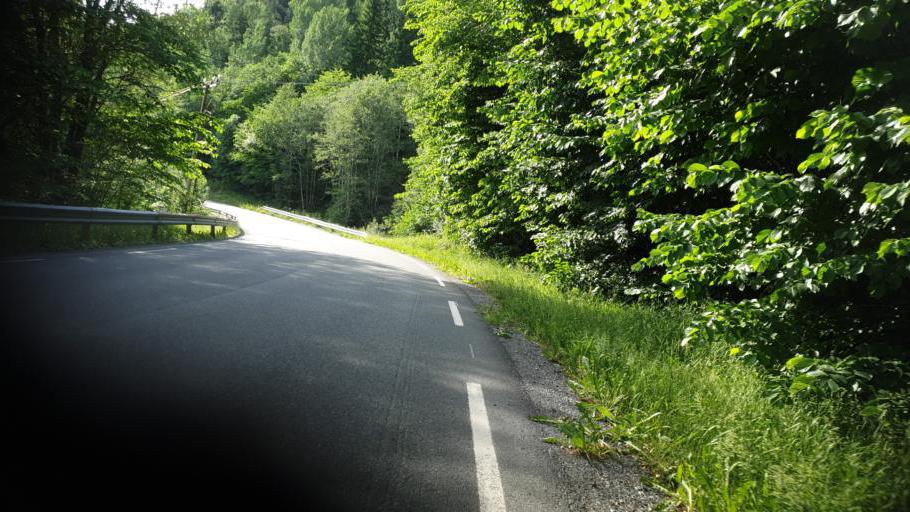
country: NO
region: Sor-Trondelag
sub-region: Trondheim
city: Trondheim
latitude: 63.5571
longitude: 10.2447
